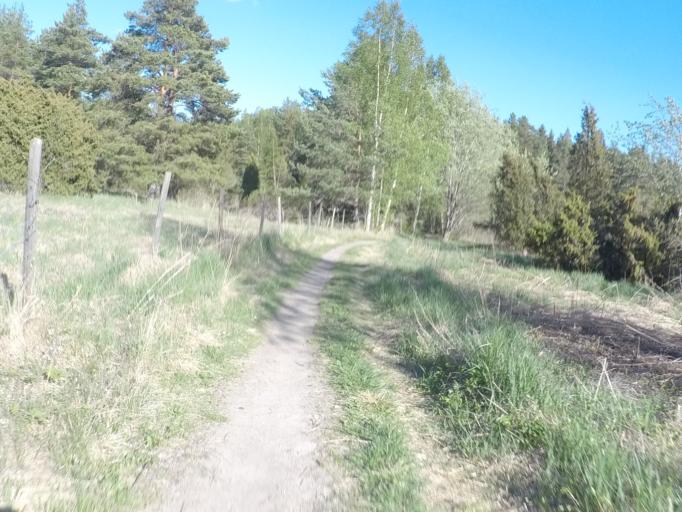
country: SE
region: Soedermanland
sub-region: Eskilstuna Kommun
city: Eskilstuna
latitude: 59.4052
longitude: 16.5333
